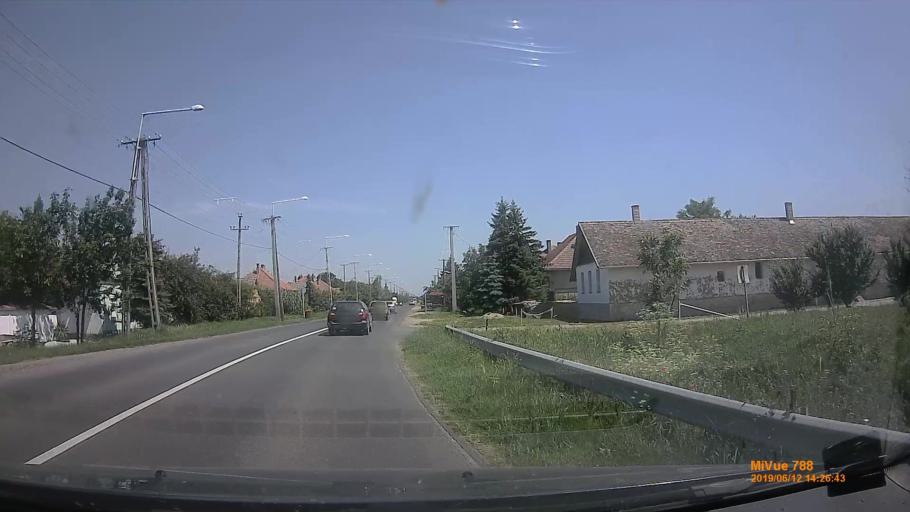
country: HU
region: Csongrad
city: Maroslele
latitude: 46.2197
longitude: 20.3475
